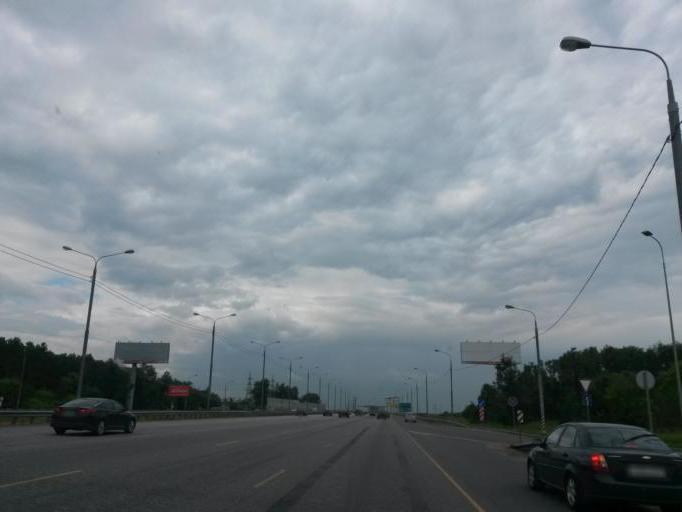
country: RU
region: Moskovskaya
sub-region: Podol'skiy Rayon
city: Podol'sk
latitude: 55.4261
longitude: 37.6131
